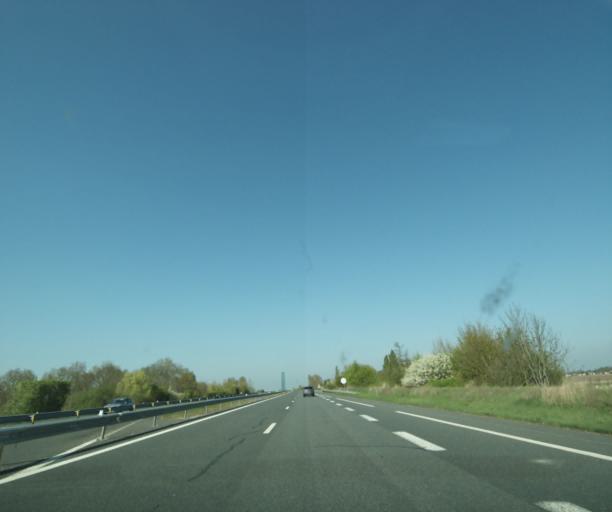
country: FR
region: Centre
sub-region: Departement du Loiret
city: Pannes
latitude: 47.9998
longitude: 2.6780
